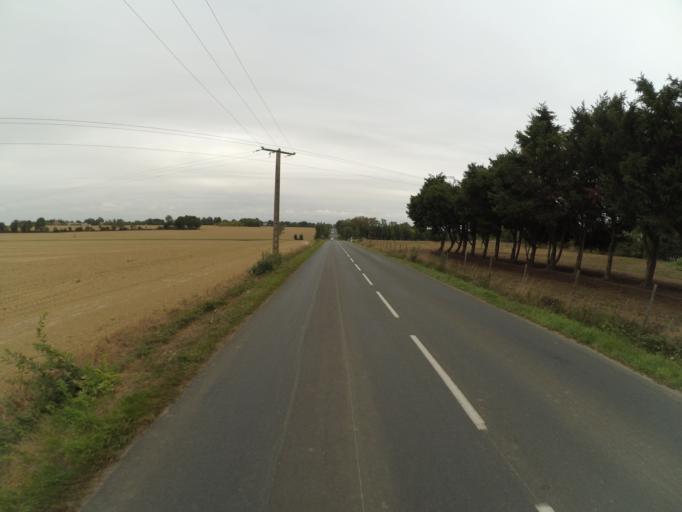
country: FR
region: Pays de la Loire
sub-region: Departement de la Vendee
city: Saint-Andre-Treize-Voies
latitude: 46.9215
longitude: -1.3931
